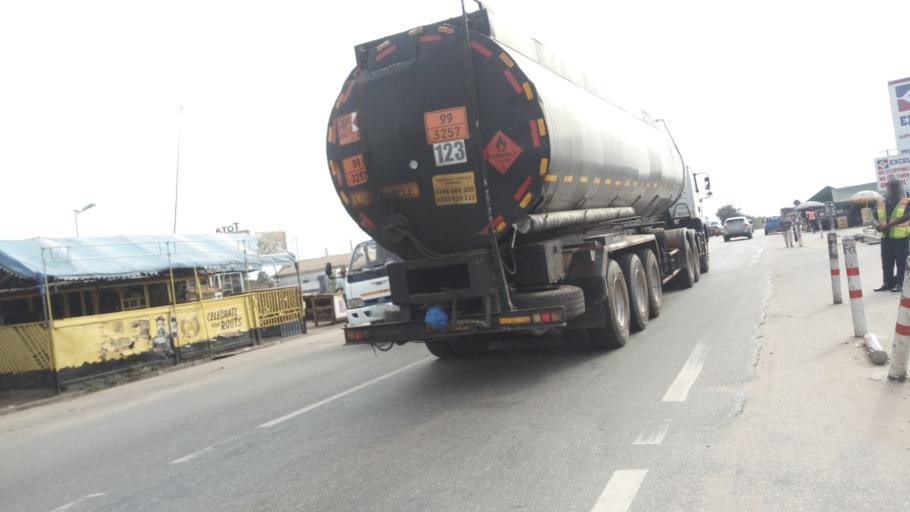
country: GH
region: Central
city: Winneba
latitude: 5.3829
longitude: -0.6439
